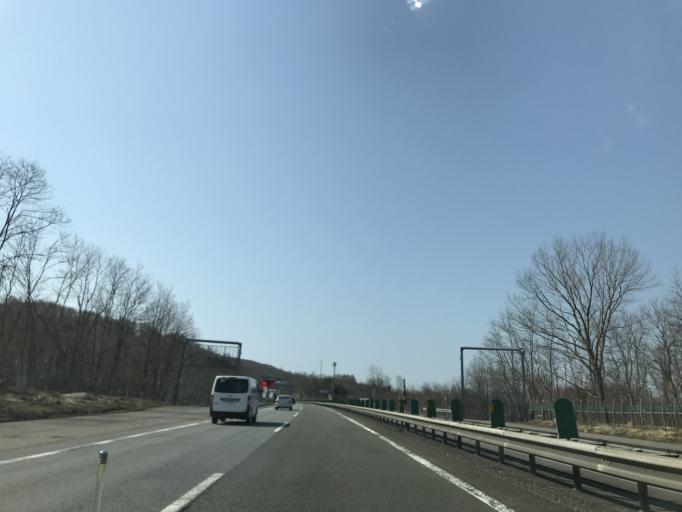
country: JP
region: Hokkaido
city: Bibai
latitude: 43.3163
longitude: 141.8834
